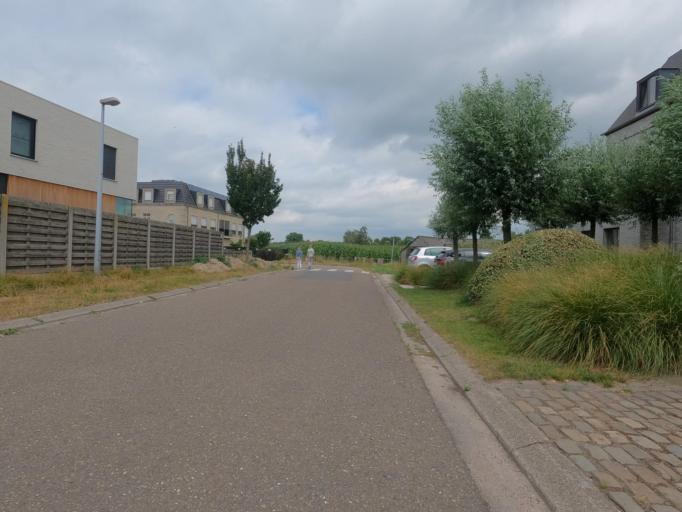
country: BE
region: Flanders
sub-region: Provincie Antwerpen
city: Hoogstraten
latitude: 51.3945
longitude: 4.7677
